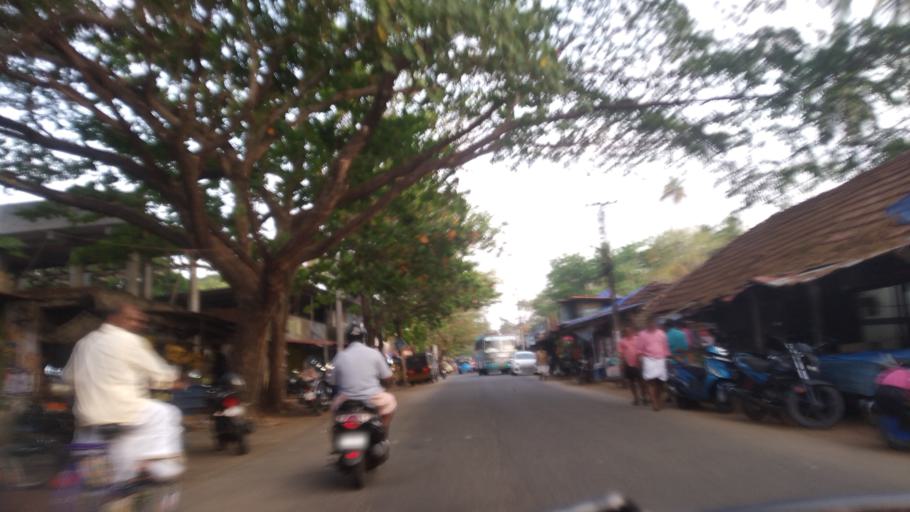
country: IN
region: Kerala
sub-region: Thrissur District
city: Kodungallur
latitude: 10.2239
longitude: 76.1571
